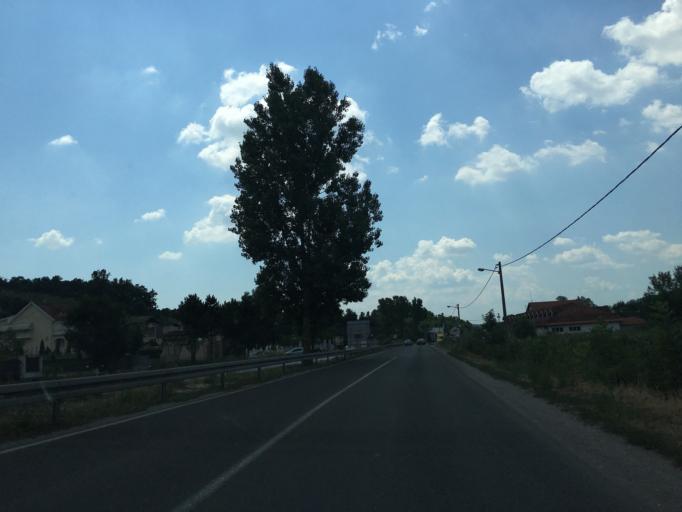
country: RS
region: Central Serbia
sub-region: Belgrade
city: Mladenovac
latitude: 44.4920
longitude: 20.6574
